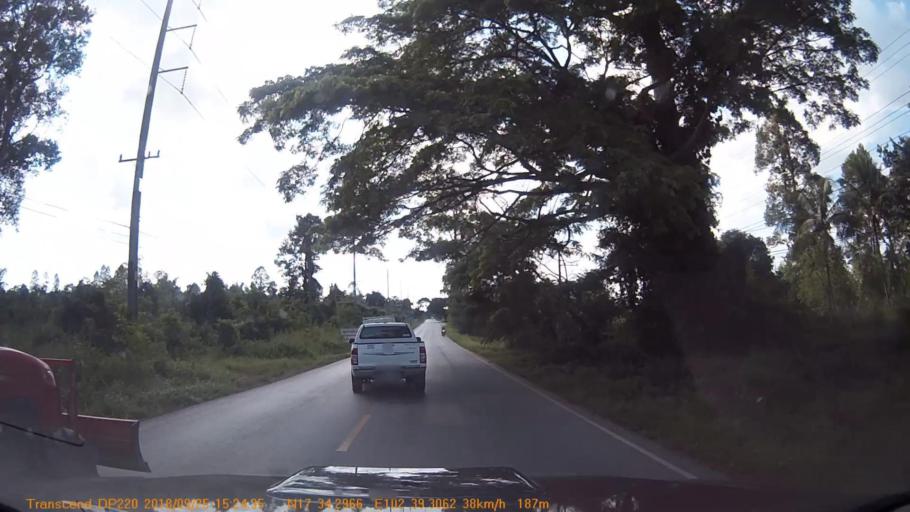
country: TH
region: Nong Khai
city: Sa Khrai
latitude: 17.5716
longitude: 102.6550
